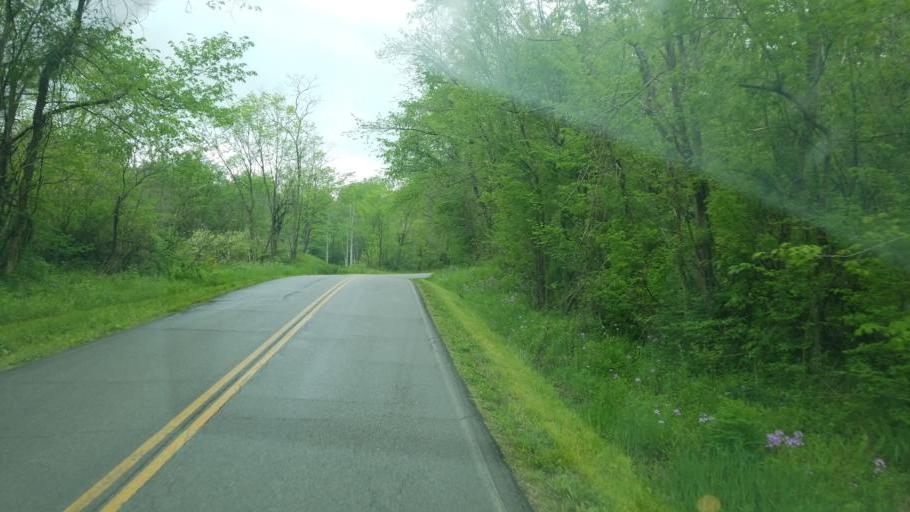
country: US
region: Ohio
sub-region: Harrison County
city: Cadiz
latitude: 40.2731
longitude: -80.9032
